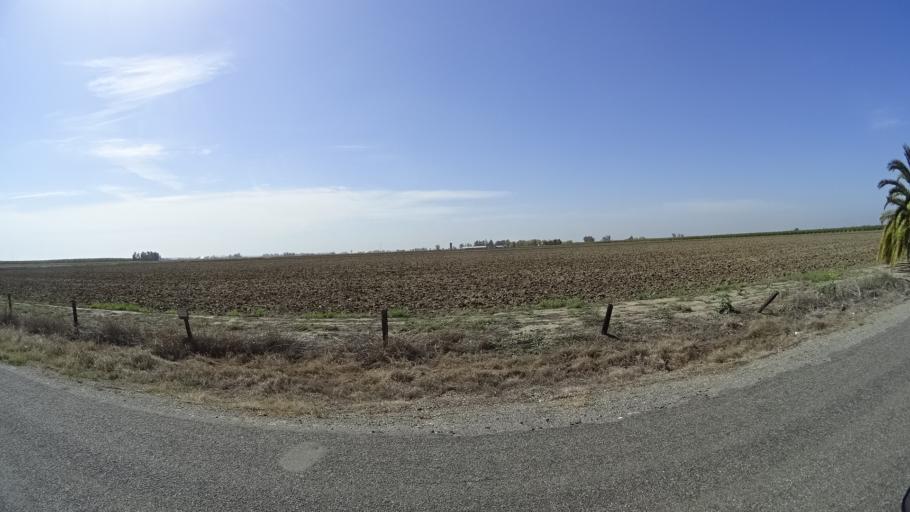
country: US
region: California
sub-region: Glenn County
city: Hamilton City
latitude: 39.6161
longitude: -122.0533
